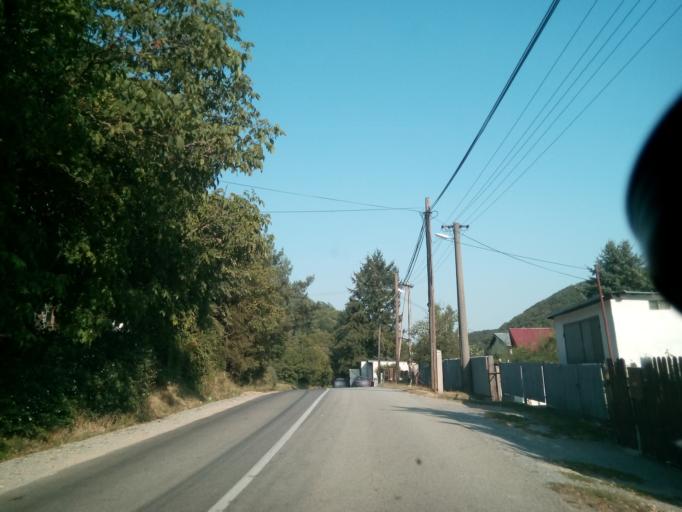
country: SK
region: Kosicky
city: Kosice
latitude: 48.7250
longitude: 21.1521
